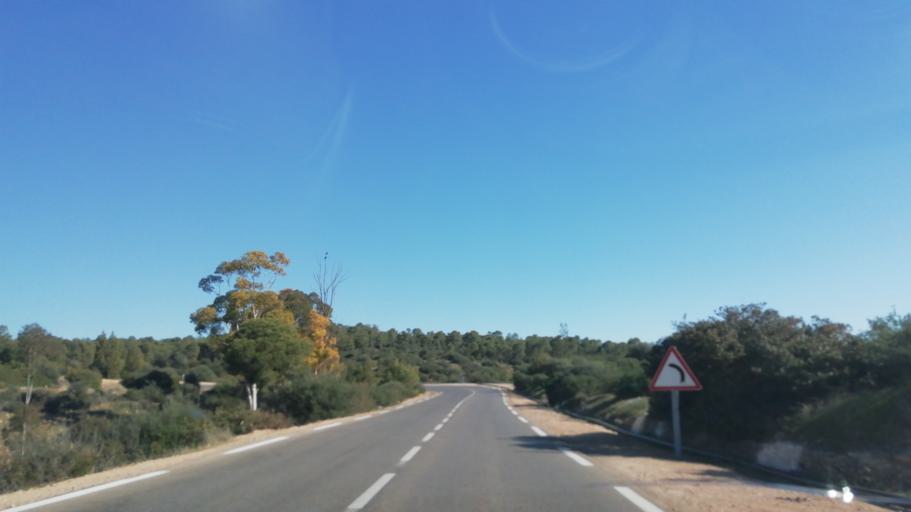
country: DZ
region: Tlemcen
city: Beni Mester
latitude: 34.8126
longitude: -1.6212
